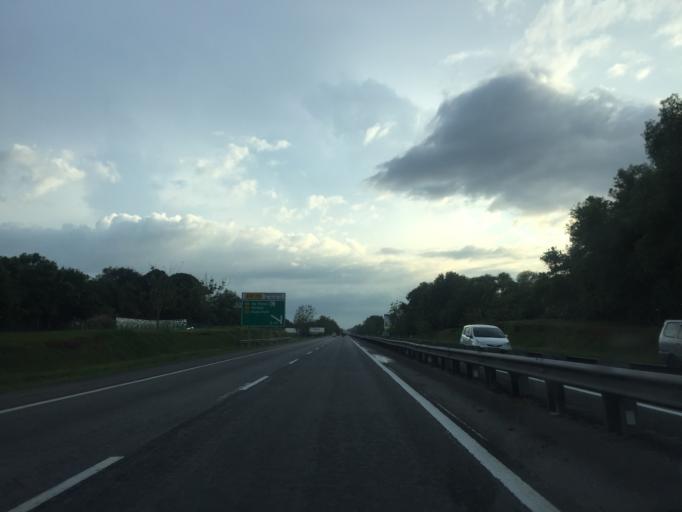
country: MY
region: Kedah
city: Bedong
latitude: 5.6942
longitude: 100.5217
